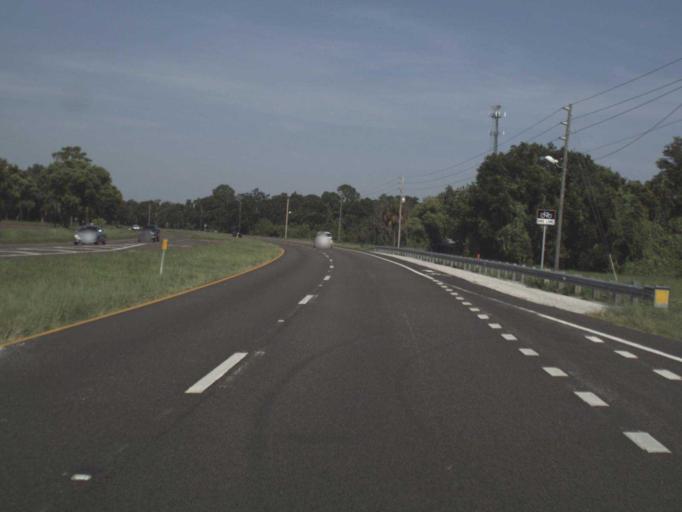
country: US
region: Florida
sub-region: Polk County
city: Willow Oak
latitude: 27.9370
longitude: -82.0887
